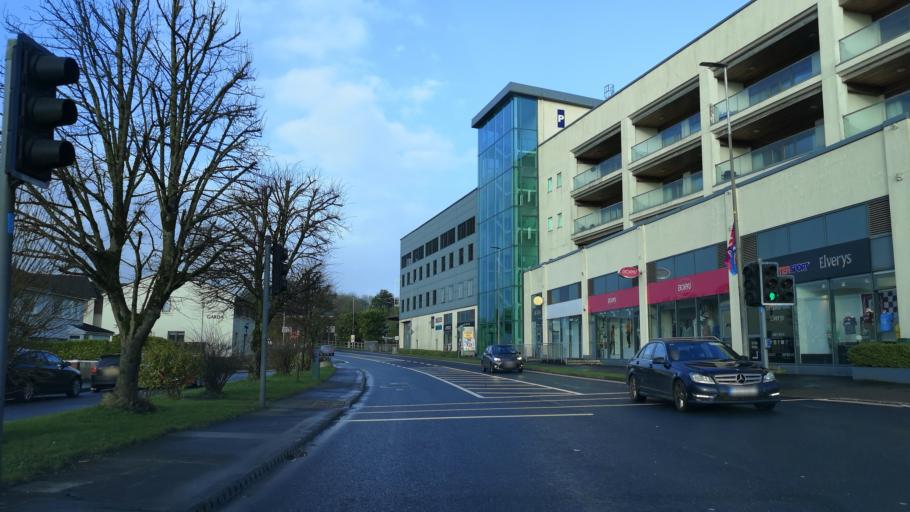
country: IE
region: Connaught
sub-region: County Galway
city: Tuam
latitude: 53.5149
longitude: -8.8557
